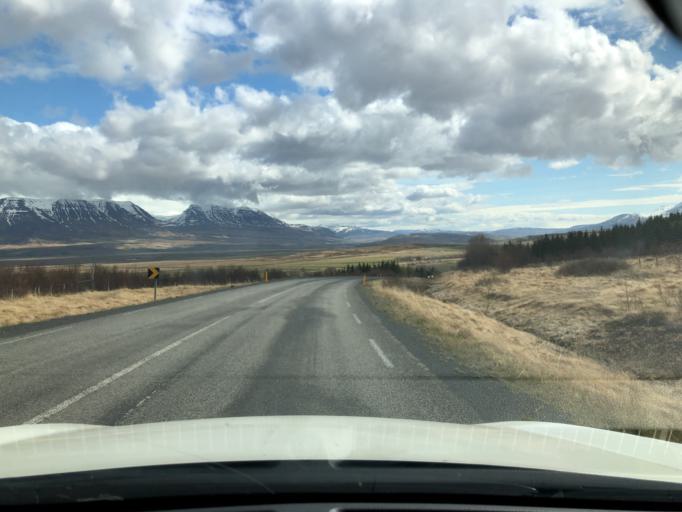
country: IS
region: Northwest
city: Saudarkrokur
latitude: 65.5487
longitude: -19.4795
